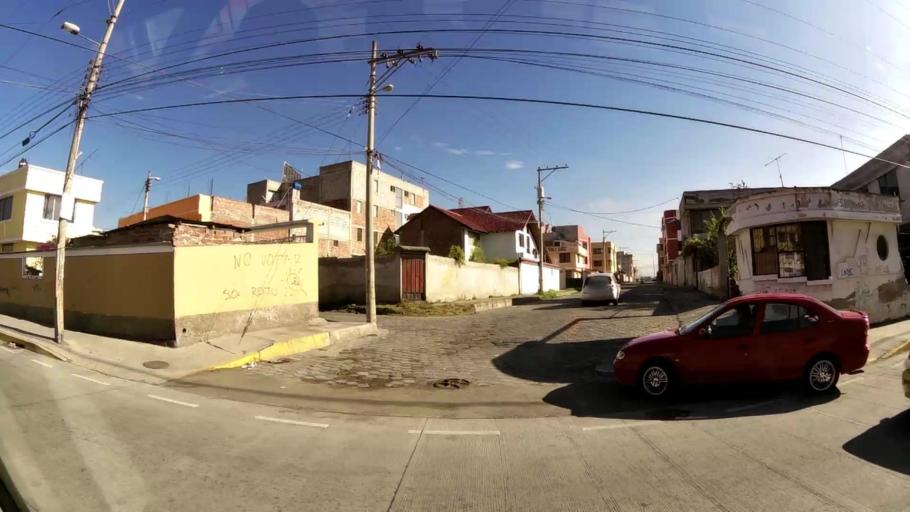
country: EC
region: Chimborazo
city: Riobamba
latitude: -1.6621
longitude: -78.6742
